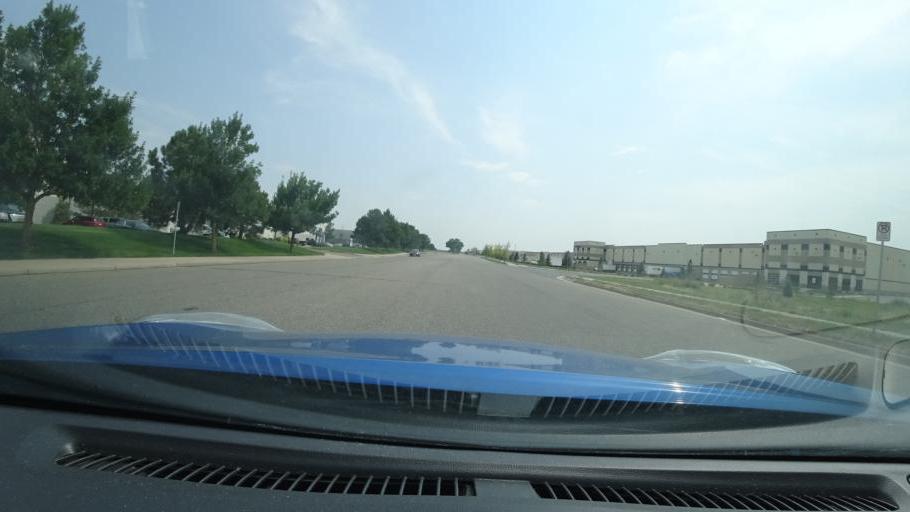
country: US
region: Colorado
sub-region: Adams County
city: Aurora
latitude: 39.7641
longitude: -104.7522
